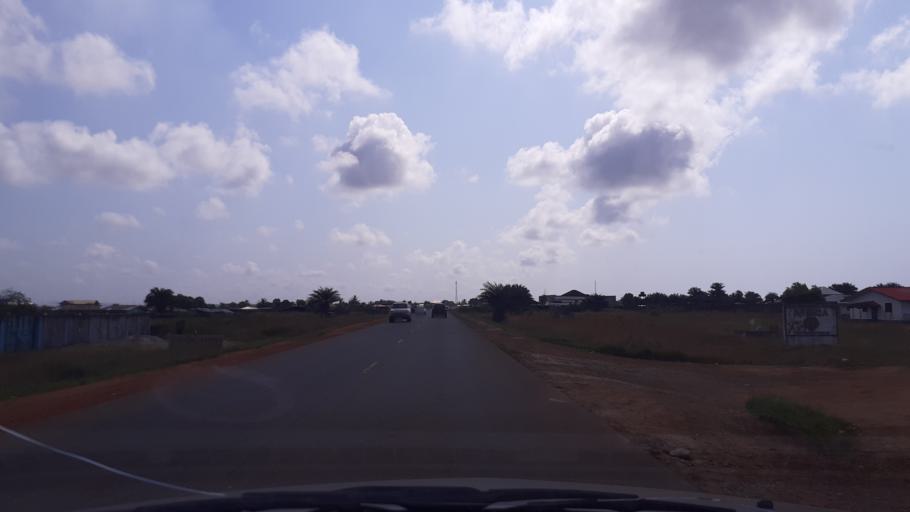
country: LR
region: Montserrado
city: Monrovia
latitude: 6.2200
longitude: -10.5928
